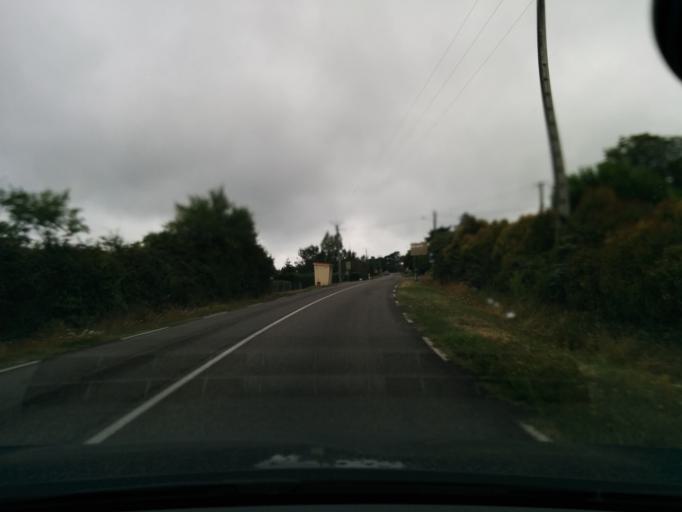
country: FR
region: Midi-Pyrenees
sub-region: Departement du Tarn-et-Garonne
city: Moissac
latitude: 44.1143
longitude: 1.0745
